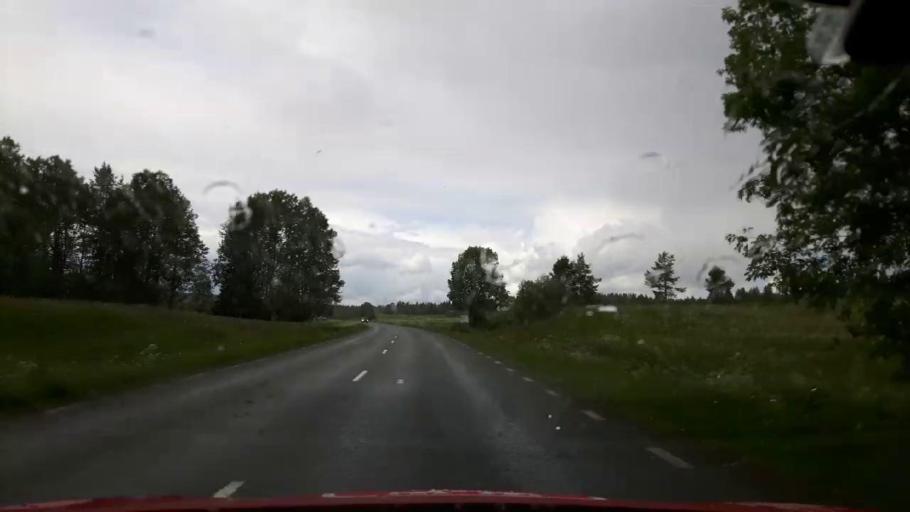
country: SE
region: Jaemtland
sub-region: Krokoms Kommun
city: Krokom
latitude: 63.4499
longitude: 14.1945
